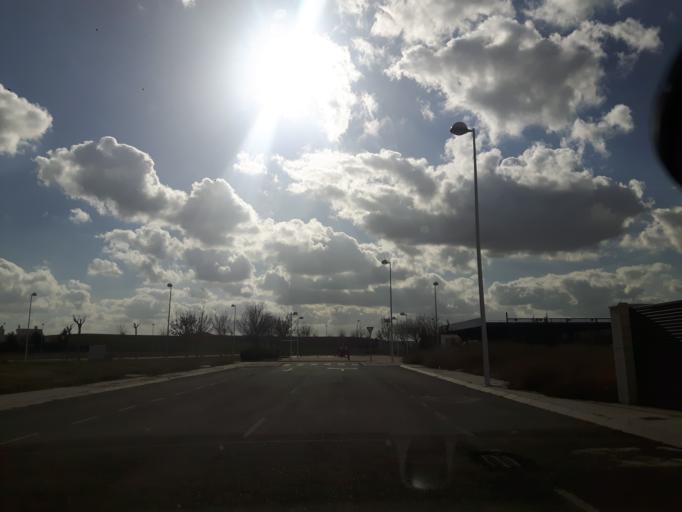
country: ES
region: Castille and Leon
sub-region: Provincia de Salamanca
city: Moriscos
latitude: 41.0071
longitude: -5.5897
